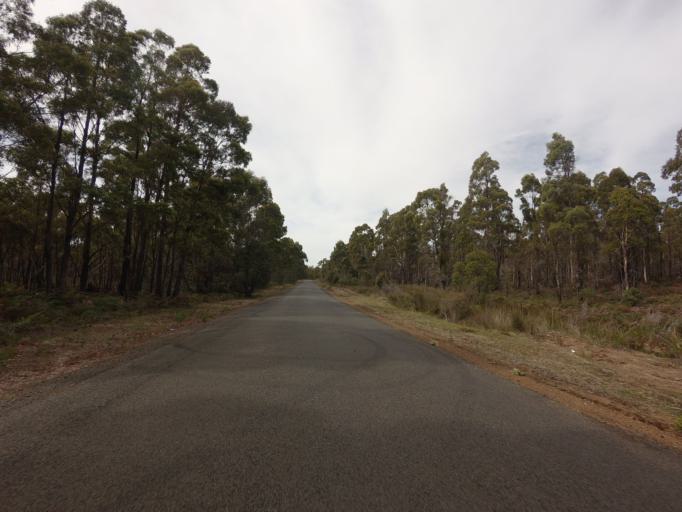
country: AU
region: Tasmania
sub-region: Sorell
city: Sorell
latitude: -42.5179
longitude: 147.6490
